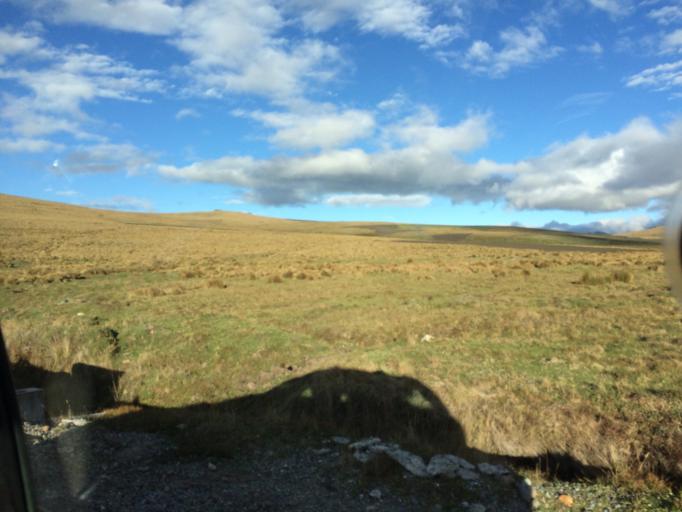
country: EC
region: Chimborazo
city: Alausi
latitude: -2.2258
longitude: -78.6875
